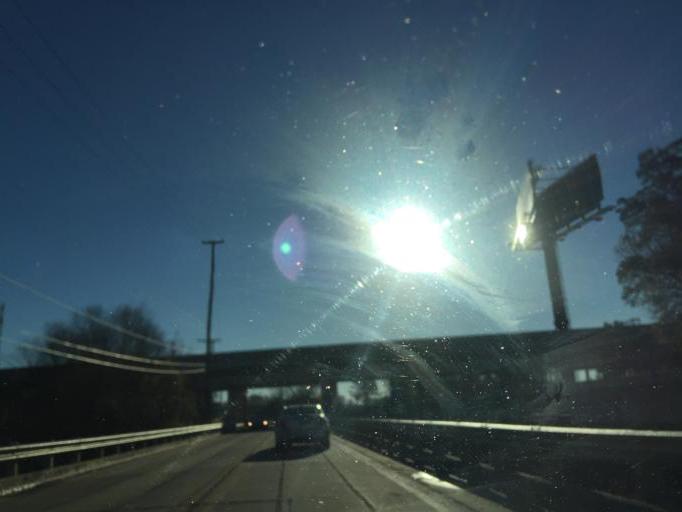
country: US
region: Mississippi
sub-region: Hinds County
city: Jackson
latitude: 32.2839
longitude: -90.1722
